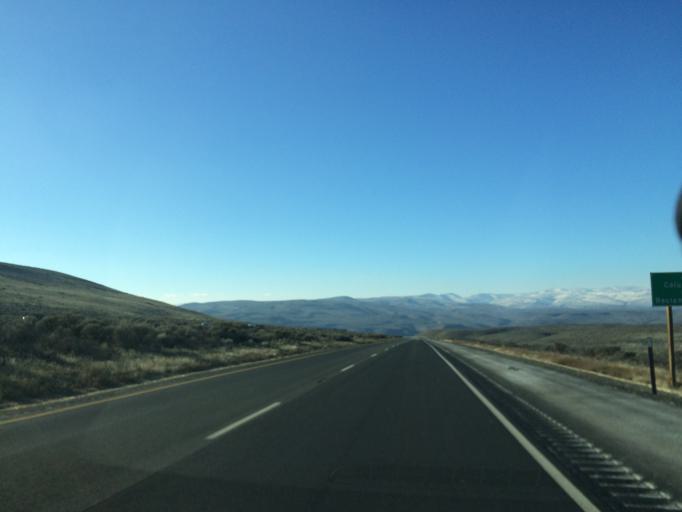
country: US
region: Washington
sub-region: Grant County
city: Quincy
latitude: 47.0072
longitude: -119.9611
